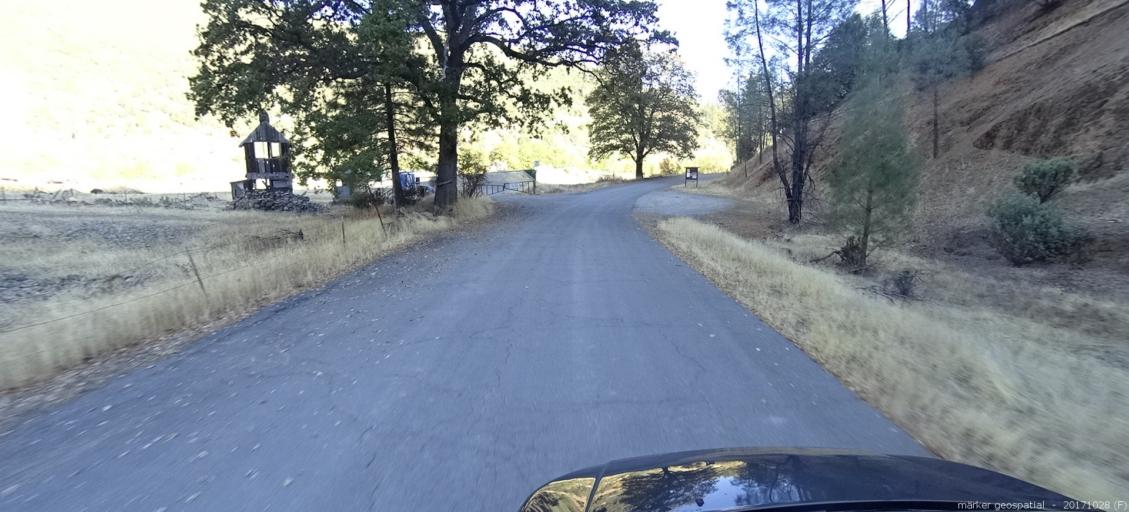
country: US
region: California
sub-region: Trinity County
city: Lewiston
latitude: 40.7146
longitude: -122.6346
